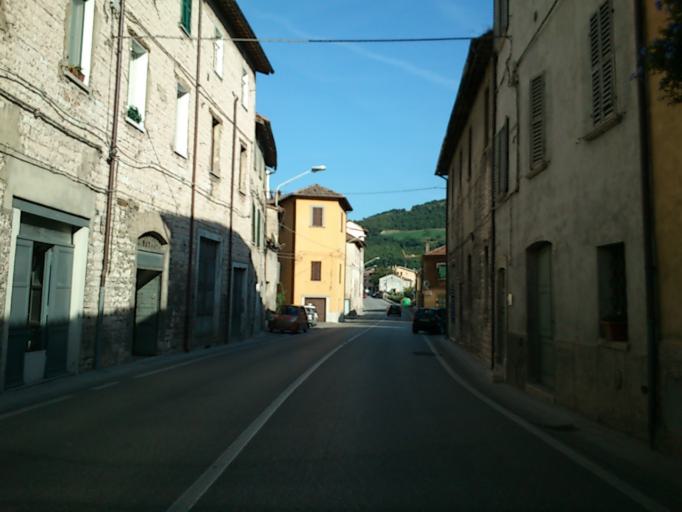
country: IT
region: The Marches
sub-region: Provincia di Pesaro e Urbino
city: Fossombrone
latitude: 43.6888
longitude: 12.8037
